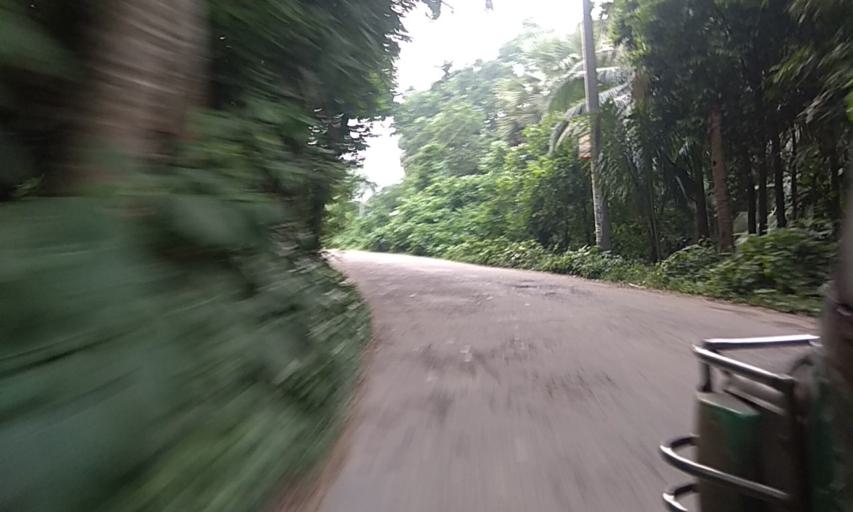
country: BD
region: Dhaka
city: Dohar
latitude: 23.4576
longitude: 90.0015
